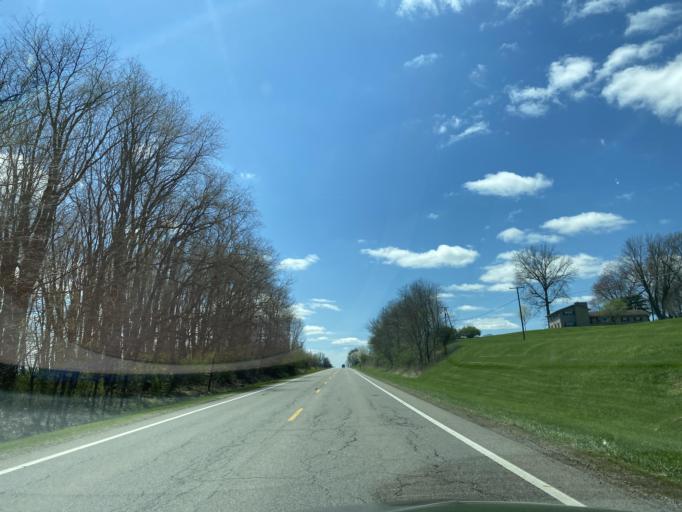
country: US
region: Ohio
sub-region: Wayne County
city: Wooster
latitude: 40.7528
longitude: -81.9802
